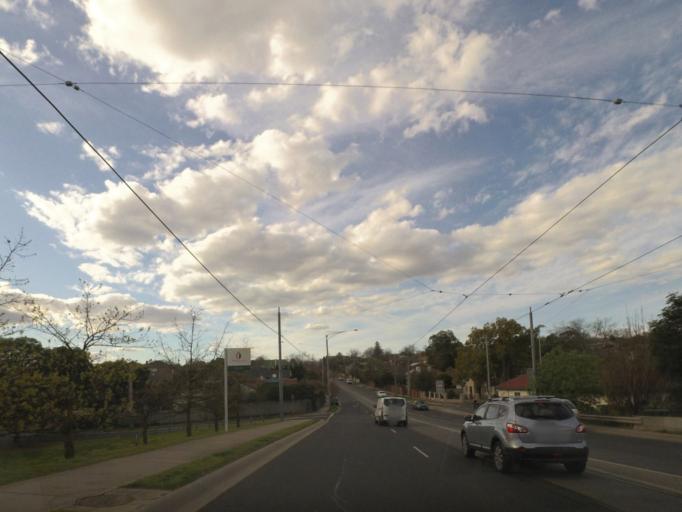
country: AU
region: Victoria
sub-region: Stonnington
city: Glen Iris
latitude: -37.8507
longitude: 145.0527
